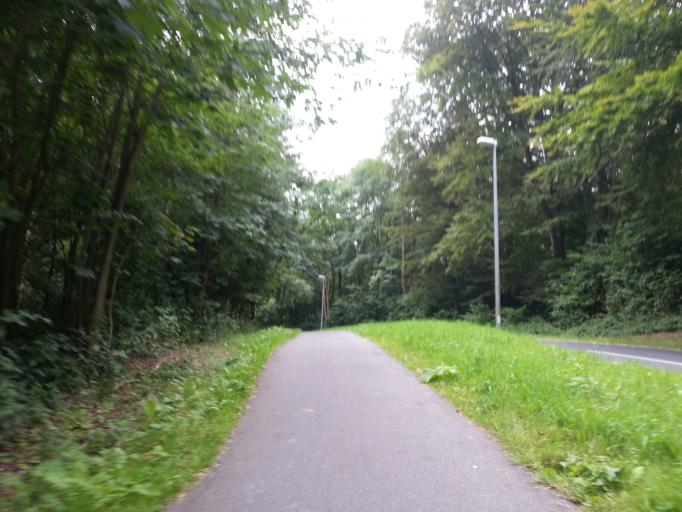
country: DK
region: South Denmark
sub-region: Kolding Kommune
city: Kolding
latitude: 55.5149
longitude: 9.4880
